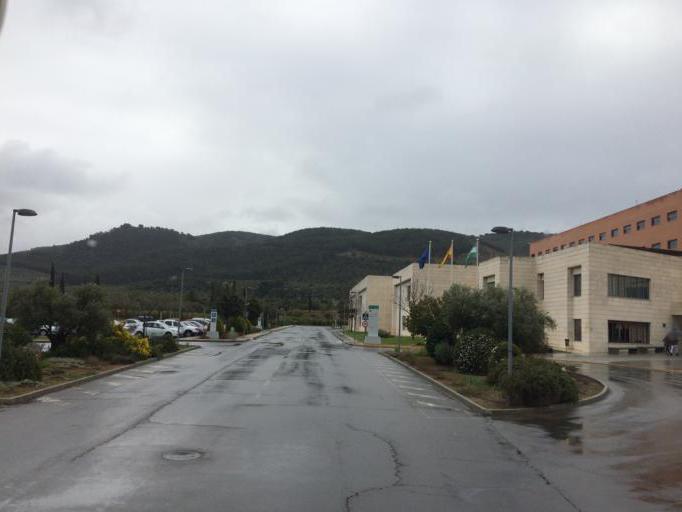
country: ES
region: Andalusia
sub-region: Provincia de Malaga
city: Antequera
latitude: 37.0315
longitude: -4.5287
